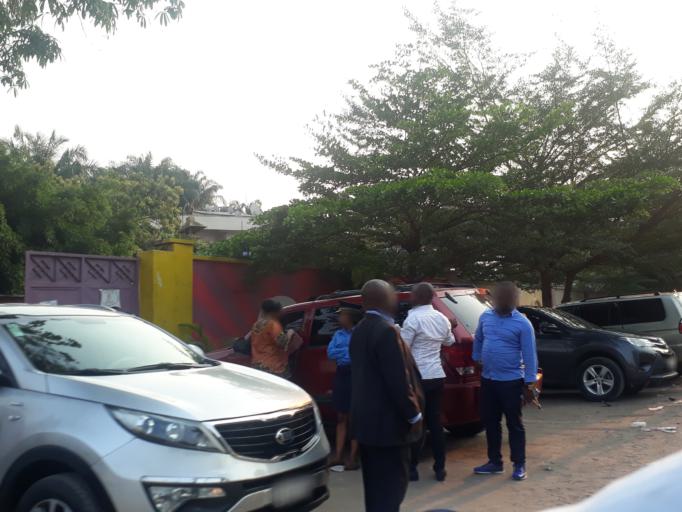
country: CD
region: Kinshasa
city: Kinshasa
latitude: -4.3095
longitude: 15.2989
